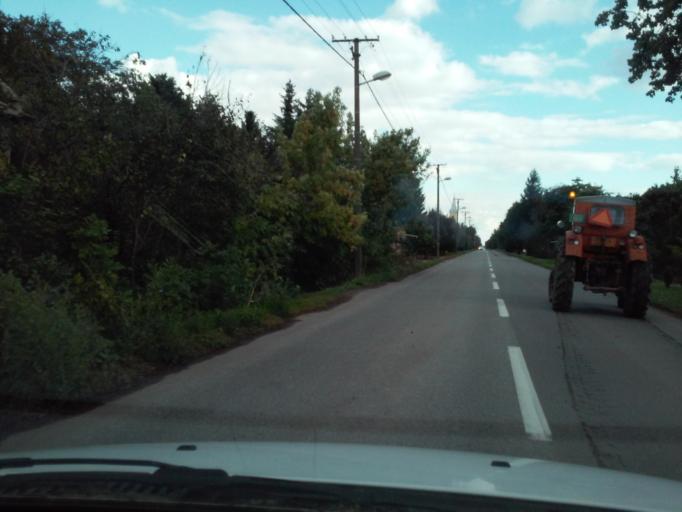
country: RS
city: Sajan
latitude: 45.8455
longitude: 20.2703
